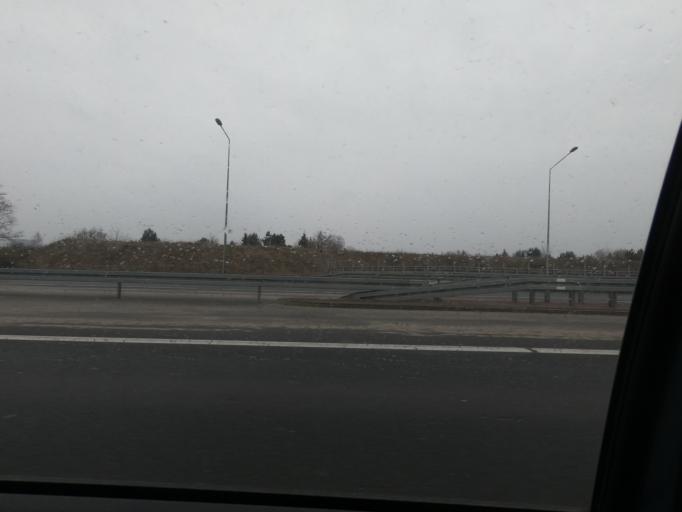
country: PL
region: Greater Poland Voivodeship
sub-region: Powiat poznanski
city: Plewiska
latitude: 52.4121
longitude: 16.8545
